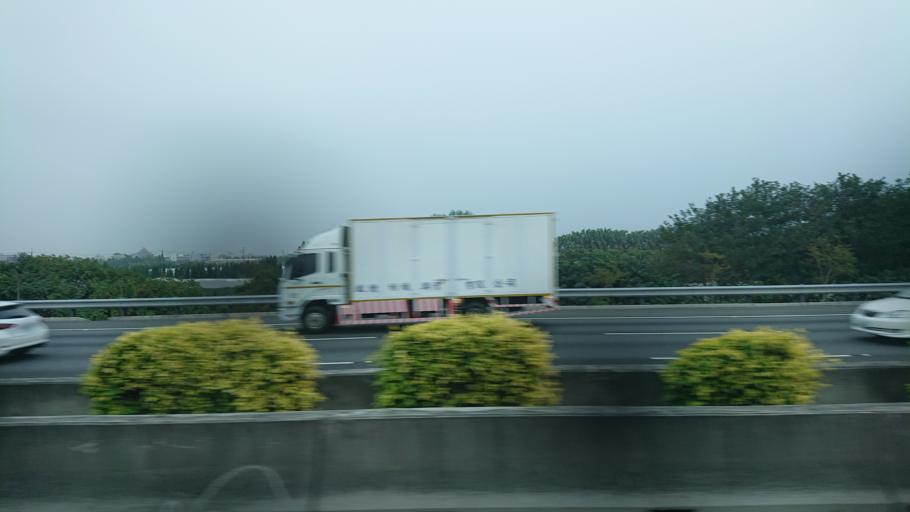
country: TW
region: Taiwan
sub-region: Nantou
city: Nantou
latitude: 23.9020
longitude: 120.4974
